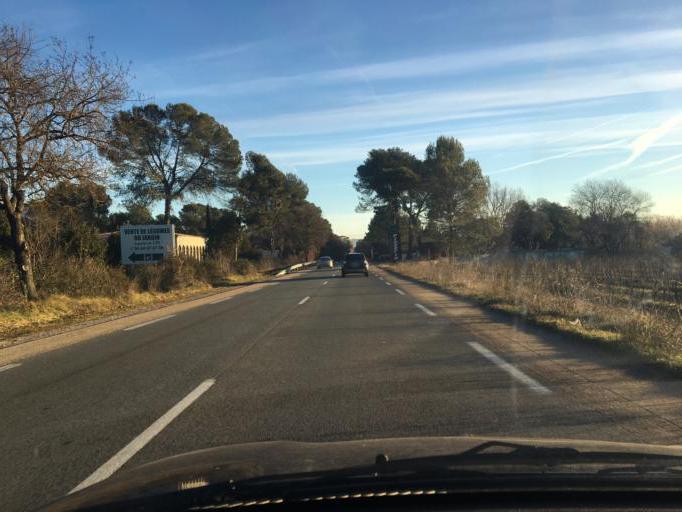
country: FR
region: Provence-Alpes-Cote d'Azur
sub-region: Departement du Var
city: La Motte
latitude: 43.4596
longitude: 6.5233
